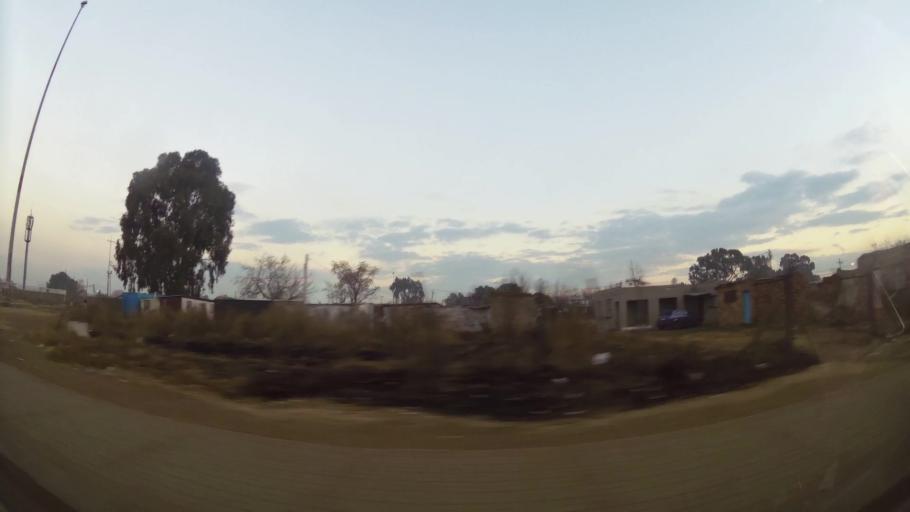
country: ZA
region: Gauteng
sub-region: City of Johannesburg Metropolitan Municipality
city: Orange Farm
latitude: -26.5482
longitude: 27.8541
